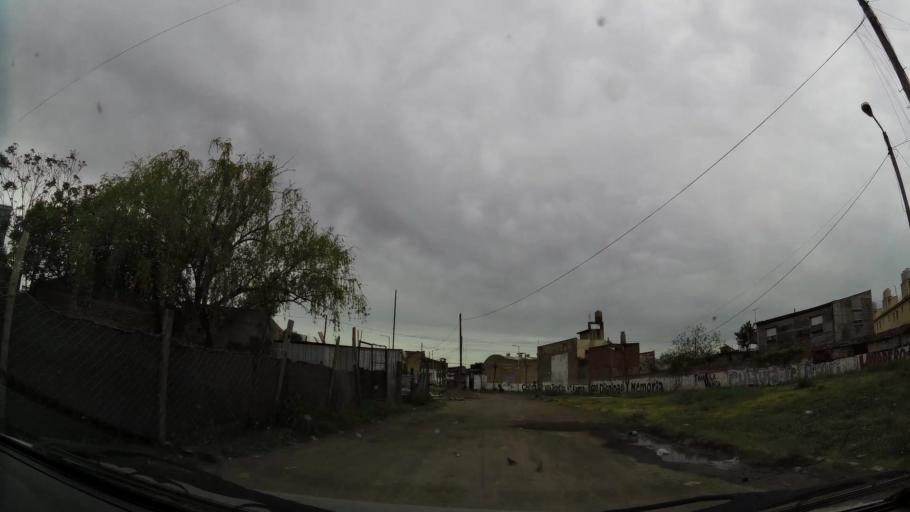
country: AR
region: Buenos Aires
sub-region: Partido de Avellaneda
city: Avellaneda
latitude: -34.6529
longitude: -58.3550
